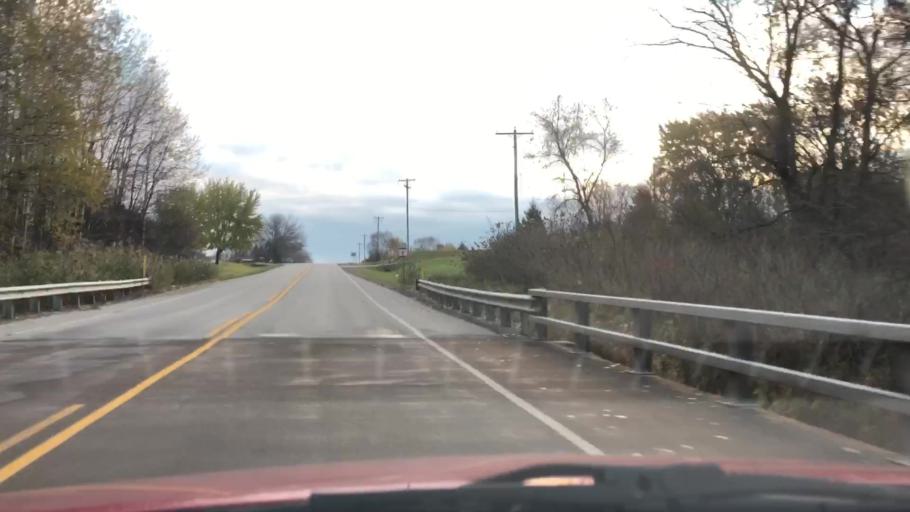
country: US
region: Wisconsin
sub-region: Brown County
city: Oneida
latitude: 44.4443
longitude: -88.2319
